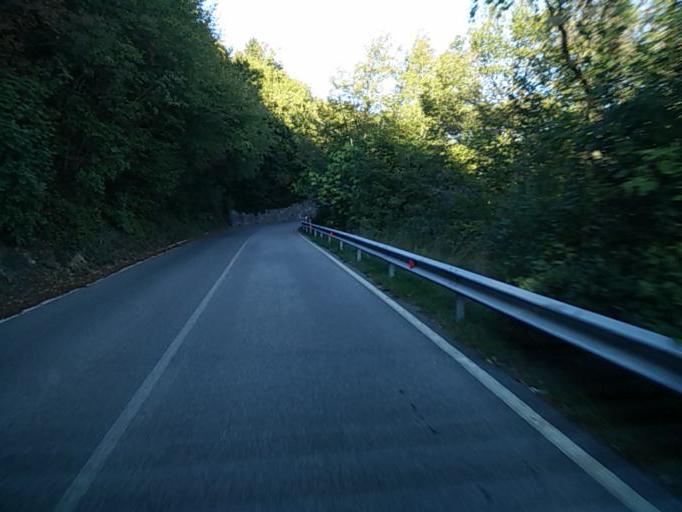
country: IT
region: Lombardy
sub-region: Provincia di Brescia
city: Gargnano
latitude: 45.6849
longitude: 10.6477
